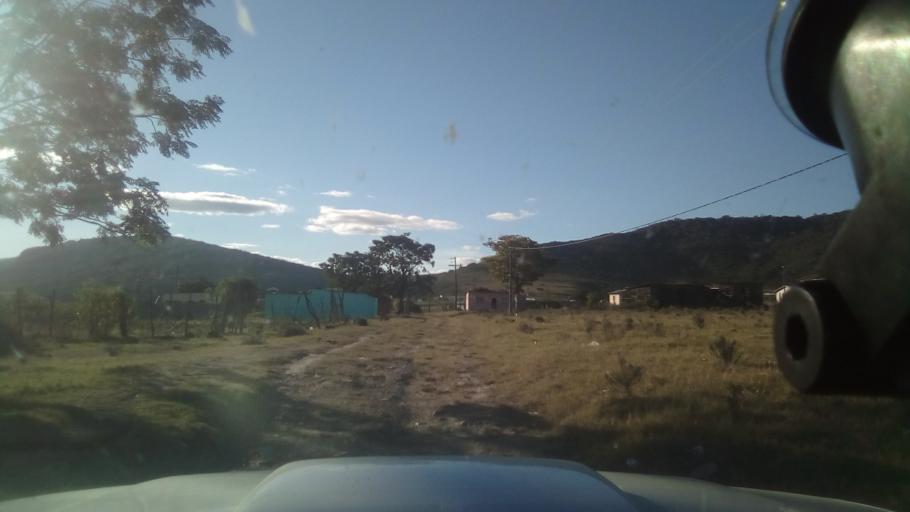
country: ZA
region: Eastern Cape
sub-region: Buffalo City Metropolitan Municipality
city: Bhisho
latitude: -32.7374
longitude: 27.3652
